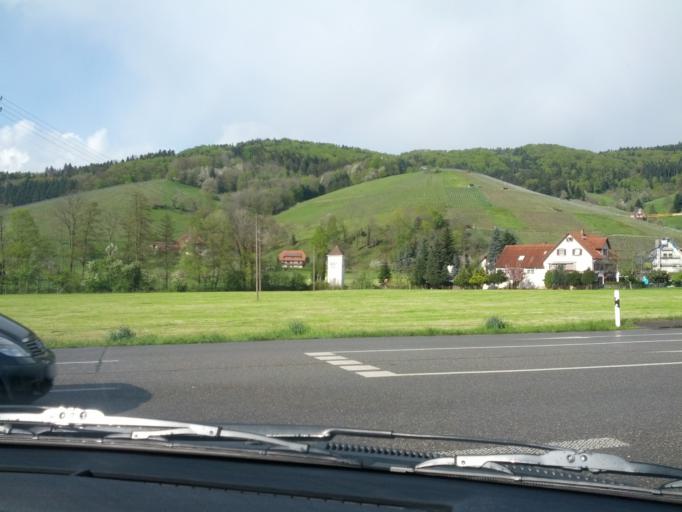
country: DE
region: Baden-Wuerttemberg
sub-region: Freiburg Region
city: Heuweiler
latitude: 48.0527
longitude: 7.9267
